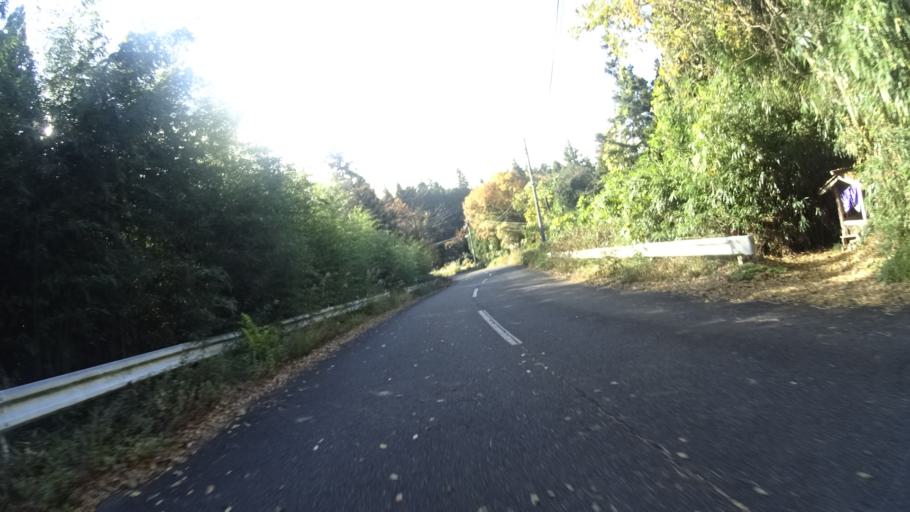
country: JP
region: Niigata
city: Yoshida-kasugacho
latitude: 37.6612
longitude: 138.8129
